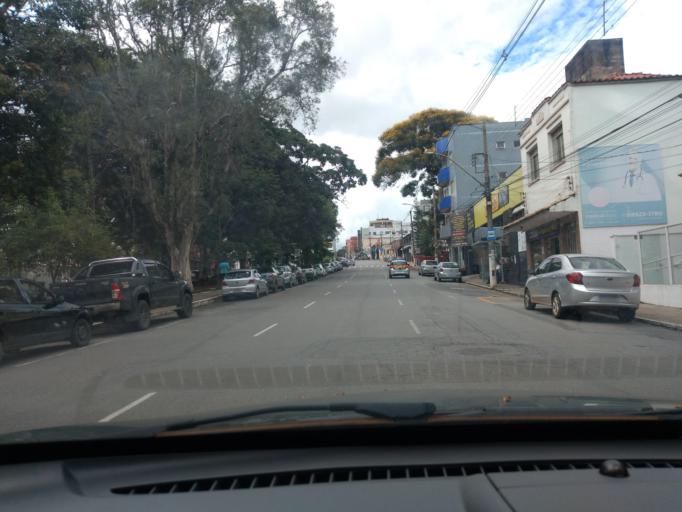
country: BR
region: Minas Gerais
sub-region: Lavras
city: Lavras
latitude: -21.2326
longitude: -44.9976
